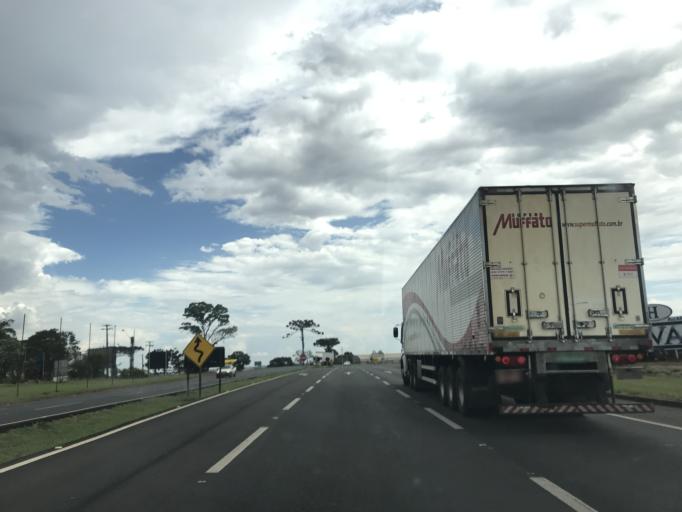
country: BR
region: Parana
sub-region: Rolandia
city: Rolandia
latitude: -23.3478
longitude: -51.3791
